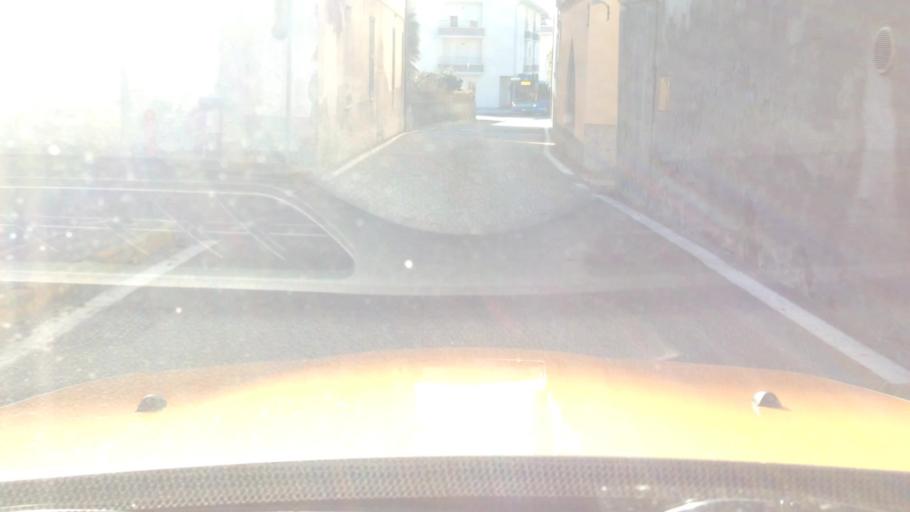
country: IT
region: Lombardy
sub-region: Provincia di Como
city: Bizzarone
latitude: 45.8353
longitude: 8.9434
